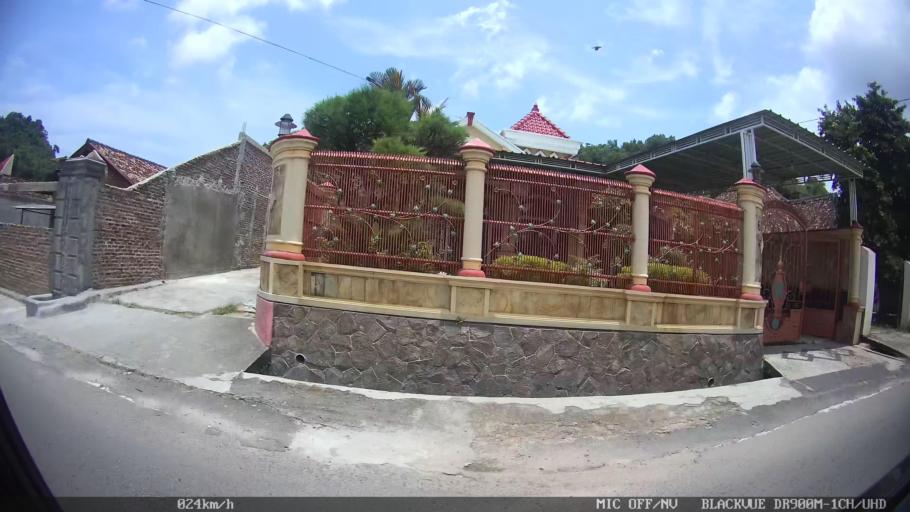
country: ID
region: Lampung
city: Kedaton
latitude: -5.3883
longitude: 105.2571
